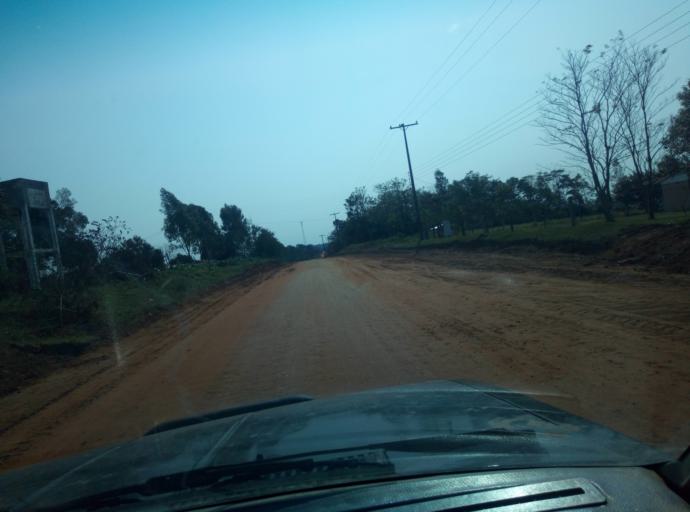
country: PY
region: Caaguazu
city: Carayao
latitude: -25.3229
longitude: -56.3295
